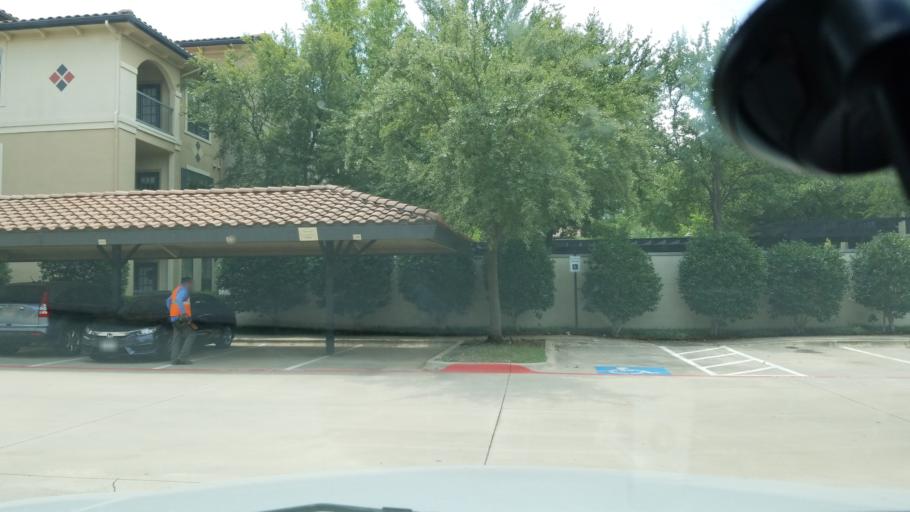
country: US
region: Texas
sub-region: Dallas County
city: Farmers Branch
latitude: 32.8976
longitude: -96.9335
